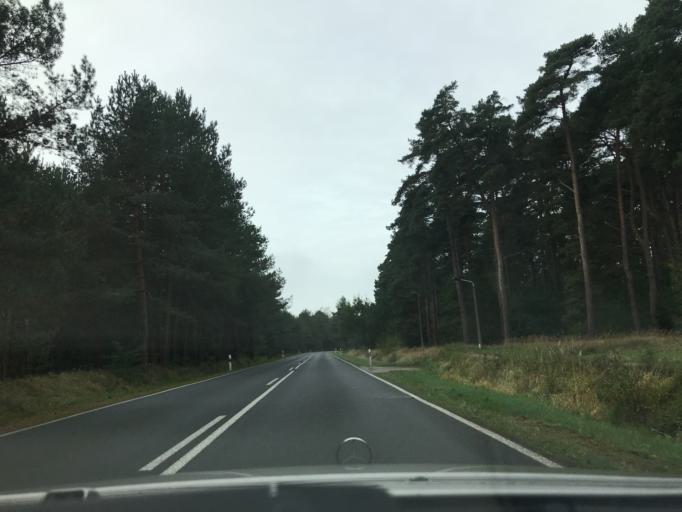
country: DE
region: Mecklenburg-Vorpommern
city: Lubmin
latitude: 54.1327
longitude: 13.6312
